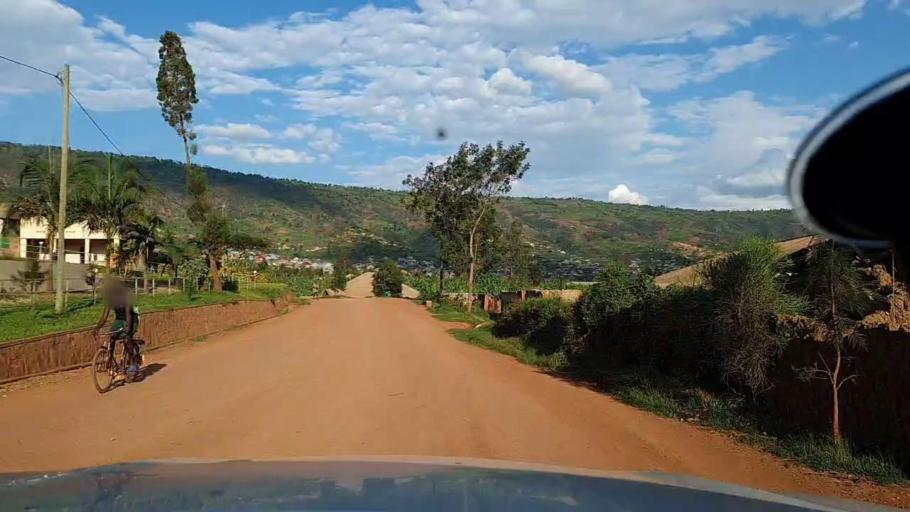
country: RW
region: Kigali
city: Kigali
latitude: -1.9031
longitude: 29.9668
